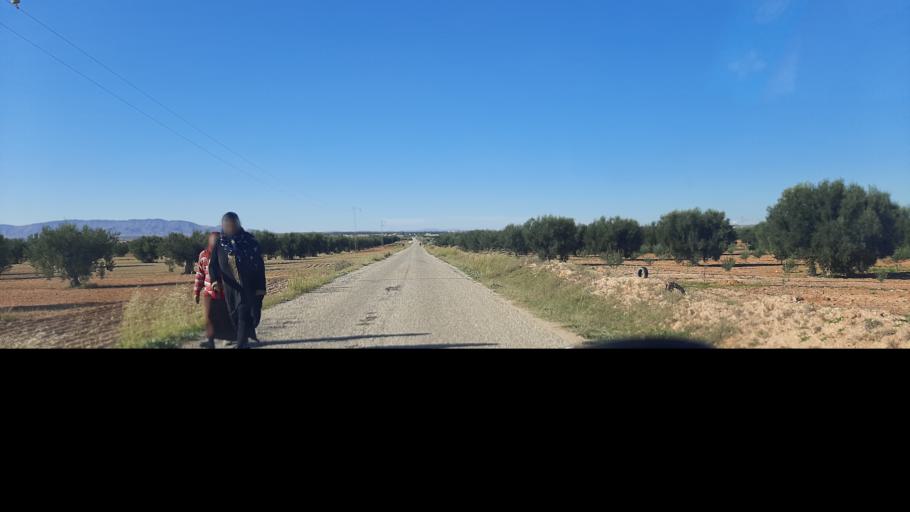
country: TN
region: Safaqis
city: Bi'r `Ali Bin Khalifah
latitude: 35.0105
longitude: 10.0842
